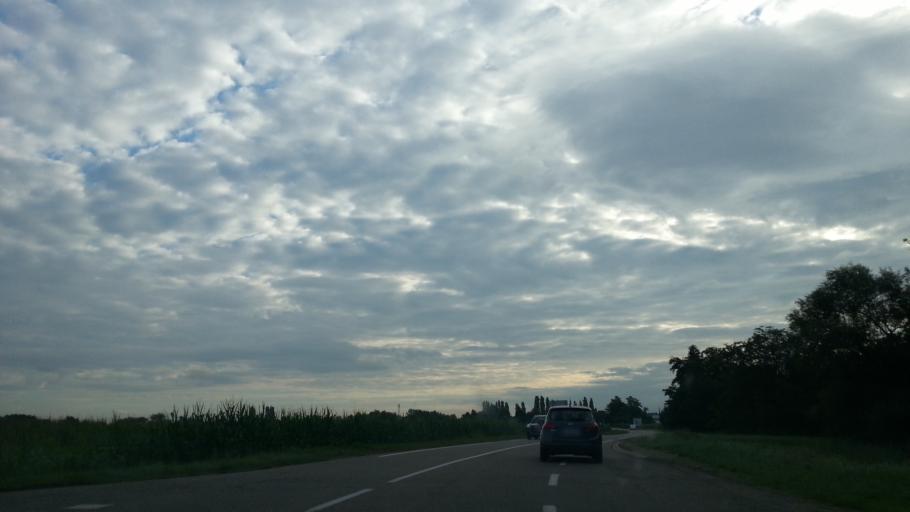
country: FR
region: Alsace
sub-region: Departement du Bas-Rhin
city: Gerstheim
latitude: 48.4088
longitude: 7.6998
